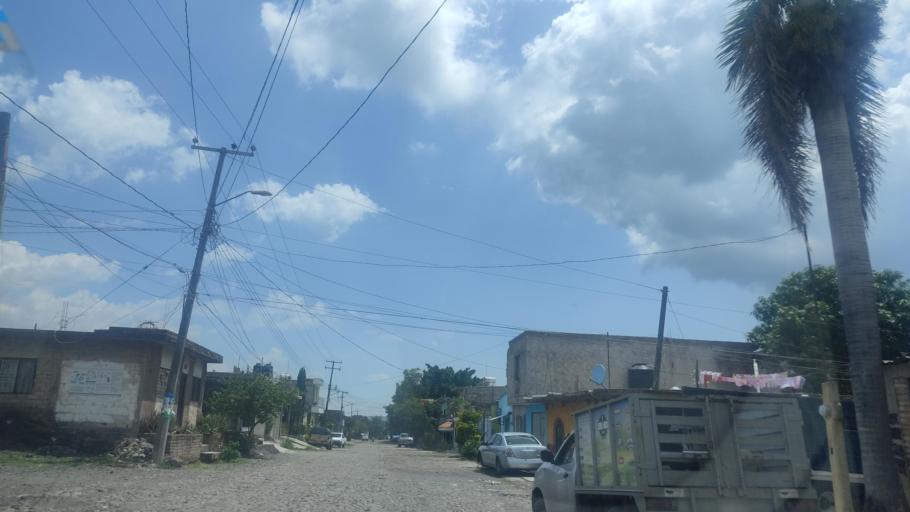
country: MX
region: Nayarit
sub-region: Tepic
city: La Corregidora
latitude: 21.4451
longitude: -104.8111
